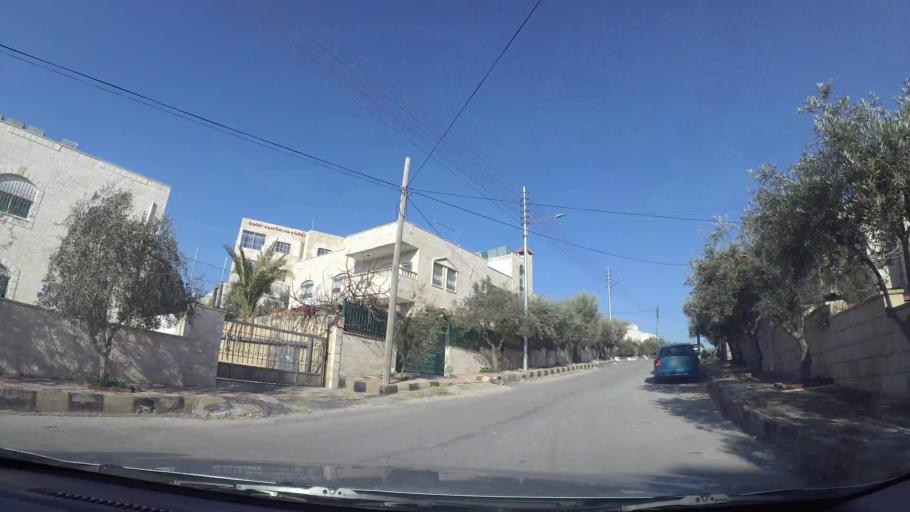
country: JO
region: Amman
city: Al Bunayyat ash Shamaliyah
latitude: 31.8986
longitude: 35.9198
